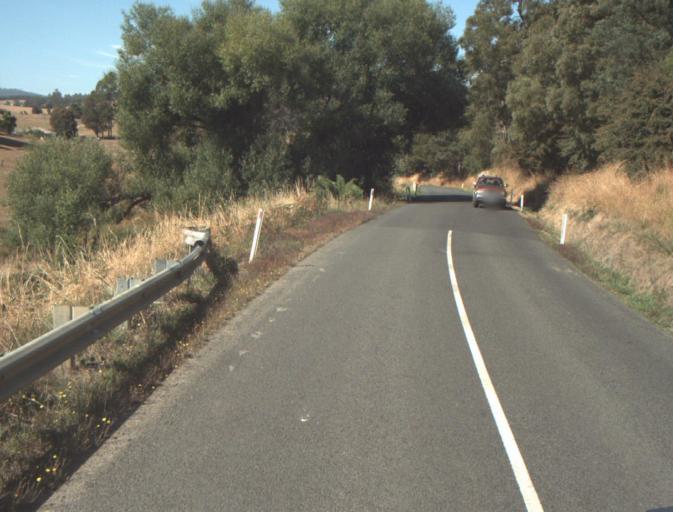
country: AU
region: Tasmania
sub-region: Launceston
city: Mayfield
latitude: -41.1836
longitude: 147.2224
